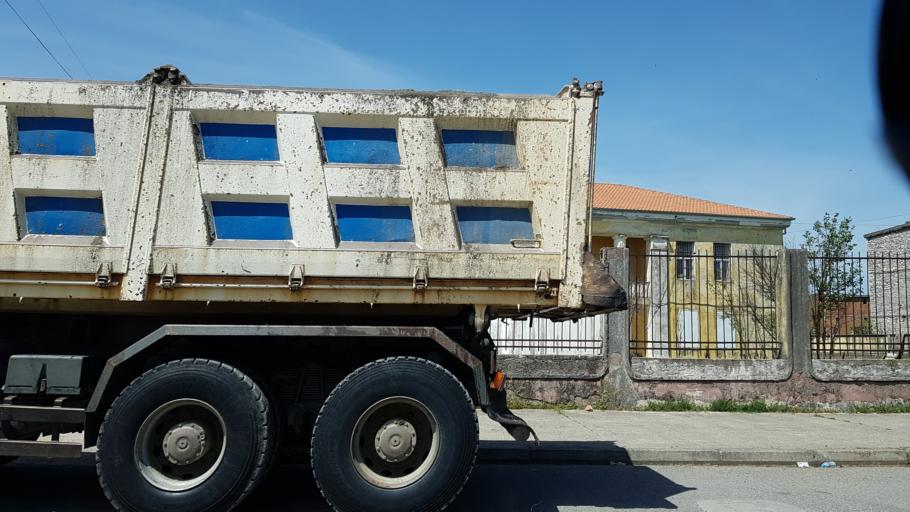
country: AL
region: Shkoder
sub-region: Rrethi i Shkodres
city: Shkoder
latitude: 42.0863
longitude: 19.5308
